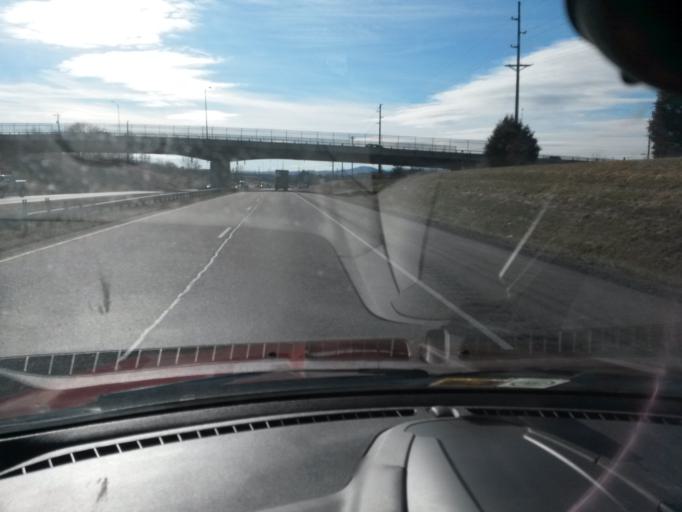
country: US
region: Virginia
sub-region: City of Harrisonburg
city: Harrisonburg
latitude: 38.4192
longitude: -78.8835
